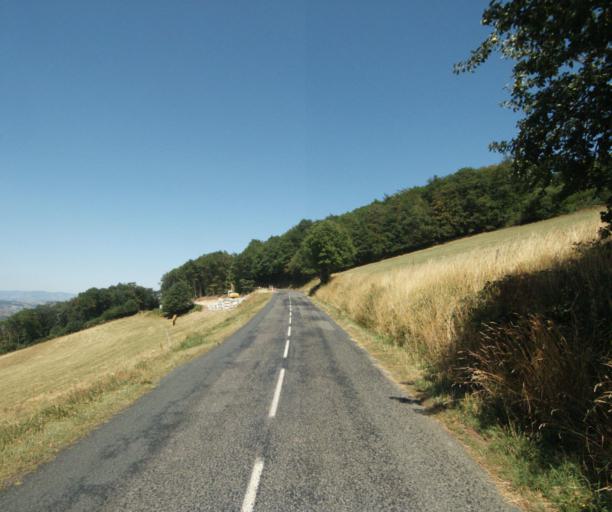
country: FR
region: Rhone-Alpes
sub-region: Departement du Rhone
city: Courzieu
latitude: 45.7215
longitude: 4.5507
